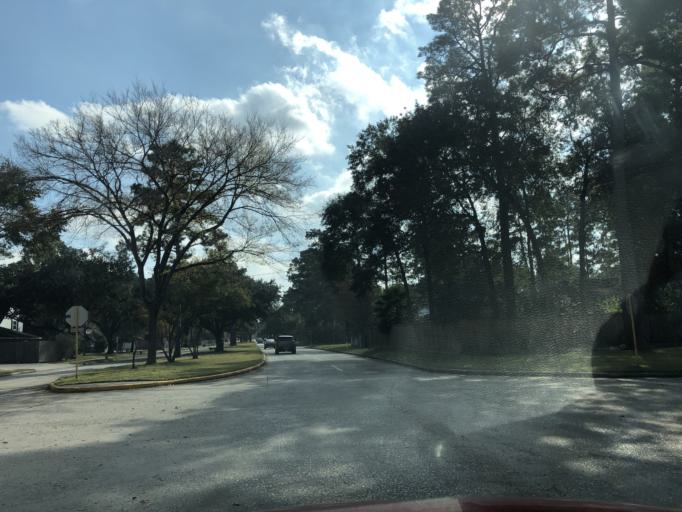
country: US
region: Texas
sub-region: Harris County
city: Tomball
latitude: 30.0294
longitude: -95.5530
